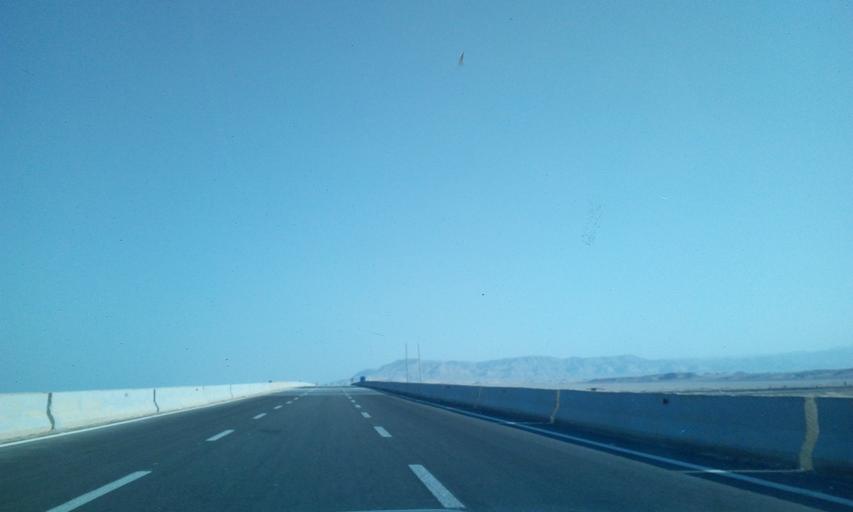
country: EG
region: As Suways
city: Ain Sukhna
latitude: 29.1120
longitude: 32.5320
